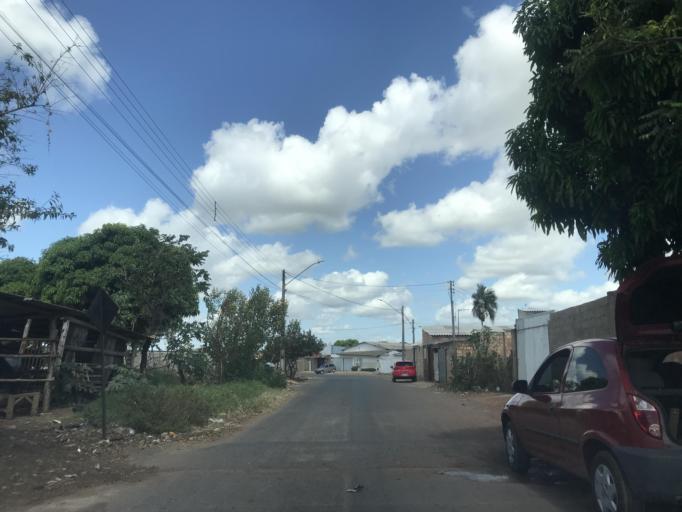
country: BR
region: Goias
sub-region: Luziania
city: Luziania
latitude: -16.2576
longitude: -47.9750
